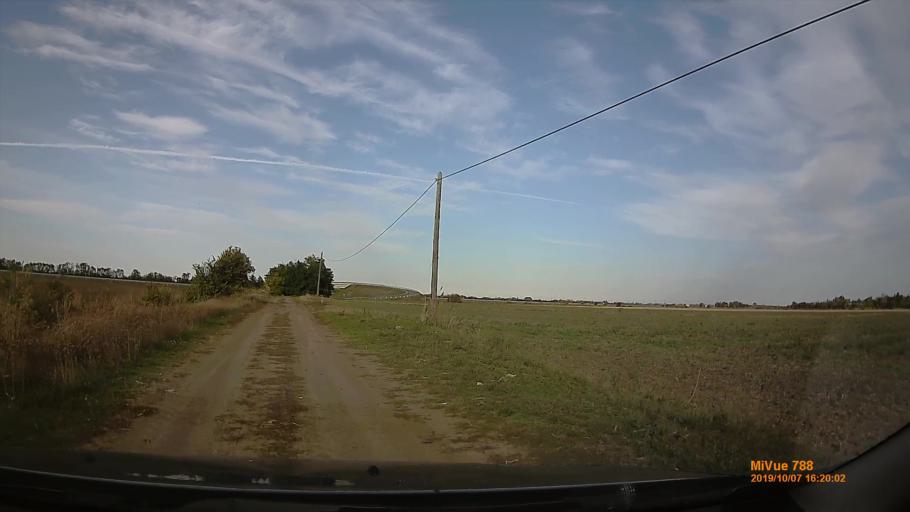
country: HU
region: Bekes
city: Szarvas
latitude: 46.8119
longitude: 20.6296
